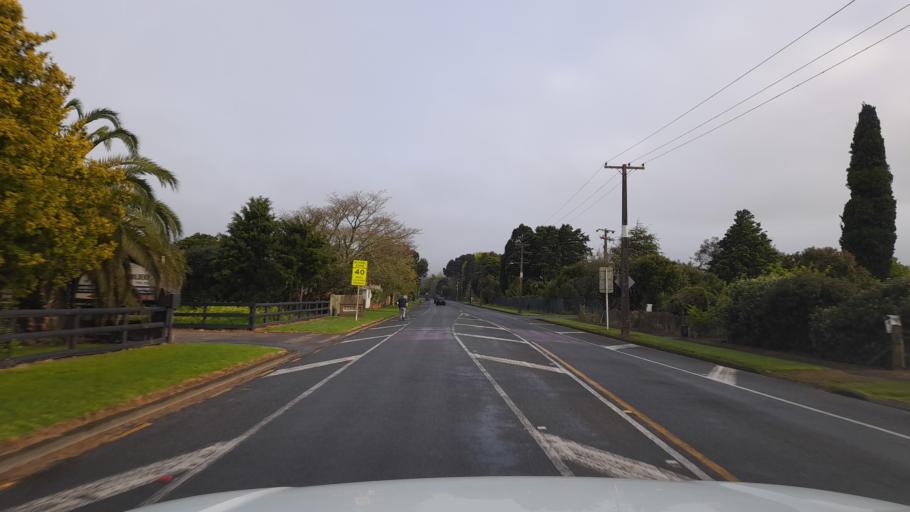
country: NZ
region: Northland
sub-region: Far North District
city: Waimate North
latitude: -35.4155
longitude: 173.8082
